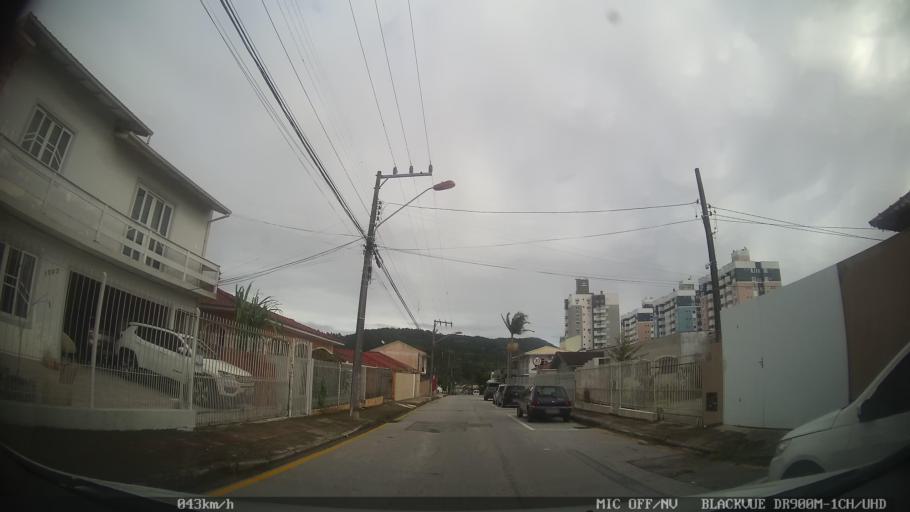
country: BR
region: Santa Catarina
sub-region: Sao Jose
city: Campinas
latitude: -27.5715
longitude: -48.6236
